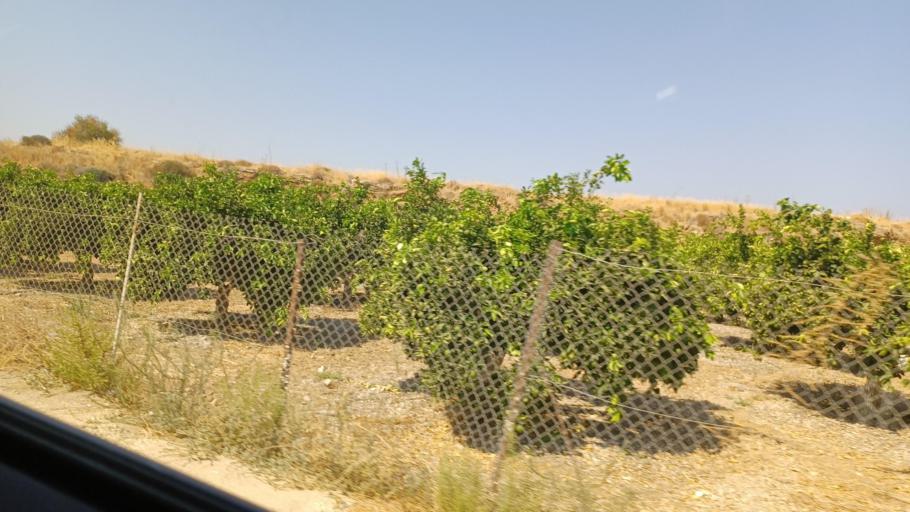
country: CY
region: Pafos
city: Polis
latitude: 35.0469
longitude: 32.4453
